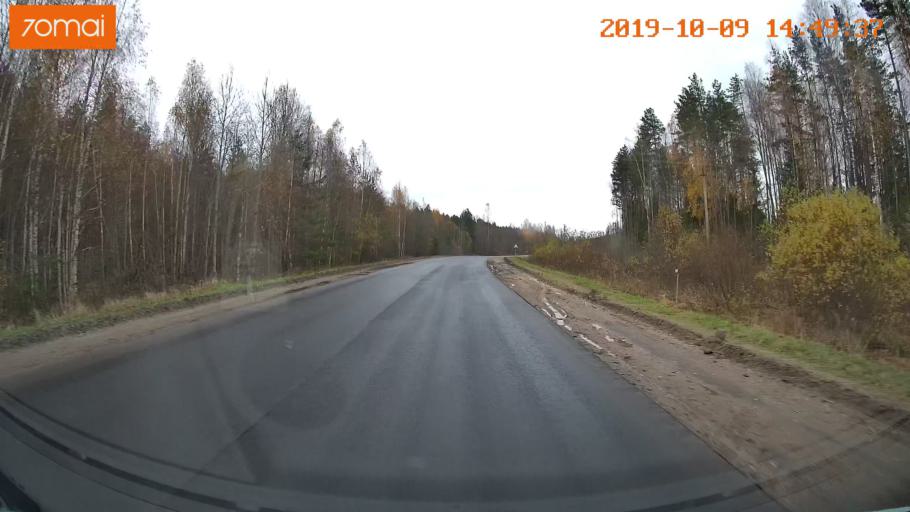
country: RU
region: Kostroma
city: Chistyye Bory
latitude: 58.3915
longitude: 41.5849
